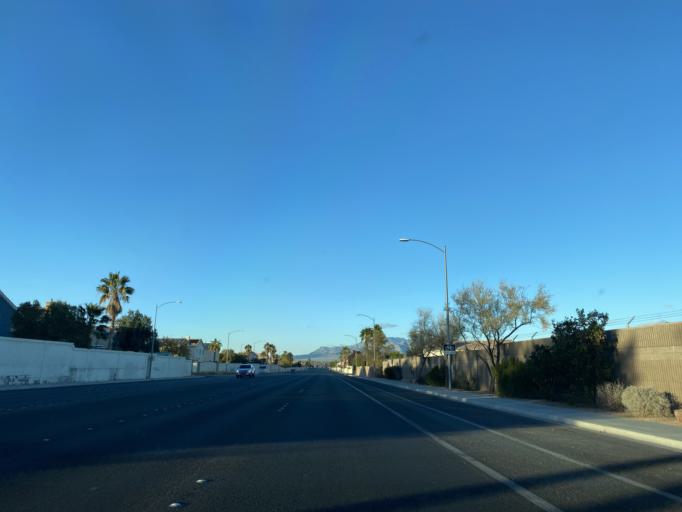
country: US
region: Nevada
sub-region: Clark County
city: Summerlin South
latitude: 36.2204
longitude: -115.2972
